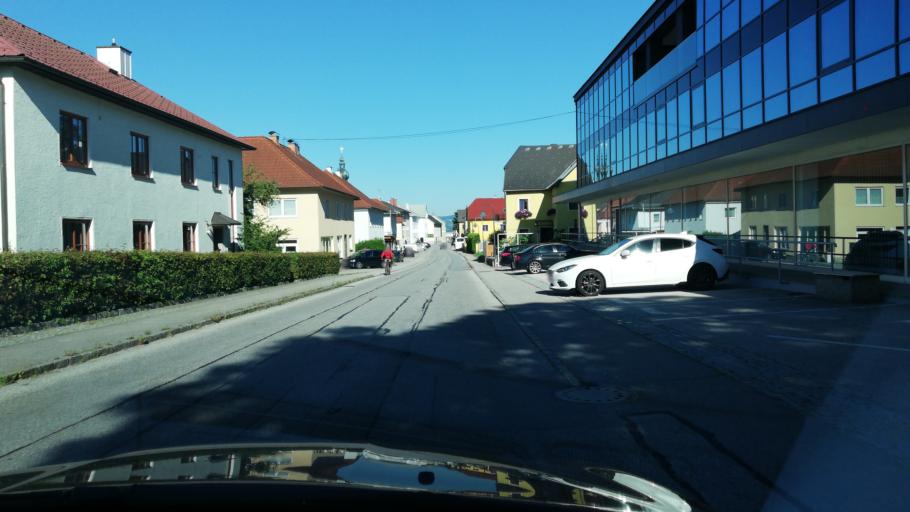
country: AT
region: Upper Austria
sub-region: Politischer Bezirk Rohrbach
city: Kleinzell im Muehlkreis
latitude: 48.4848
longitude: 13.9731
